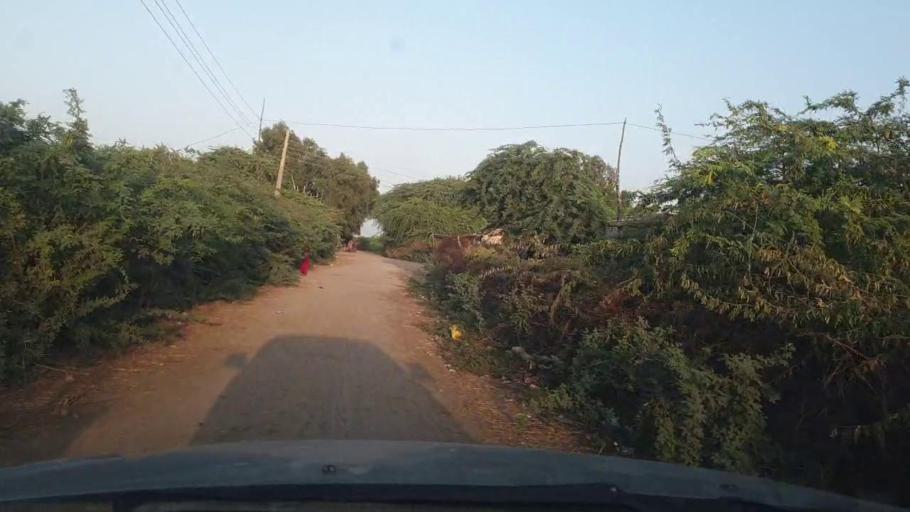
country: PK
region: Sindh
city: Tando Ghulam Ali
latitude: 25.1586
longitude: 68.9712
